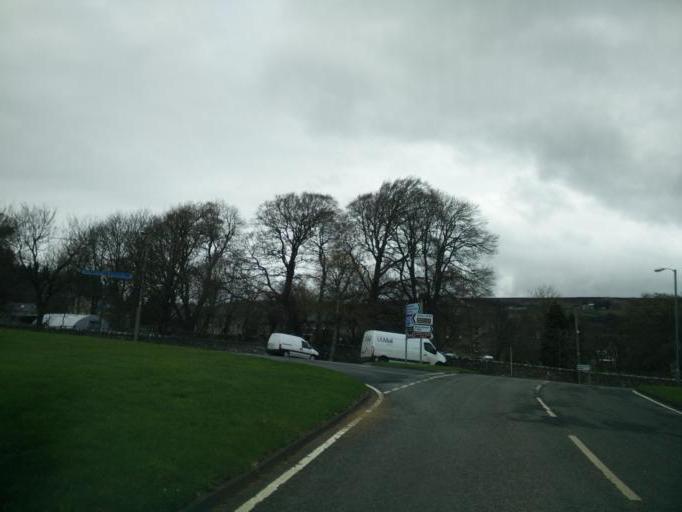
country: GB
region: England
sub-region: County Durham
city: Stanhope
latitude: 54.7484
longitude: -2.0185
